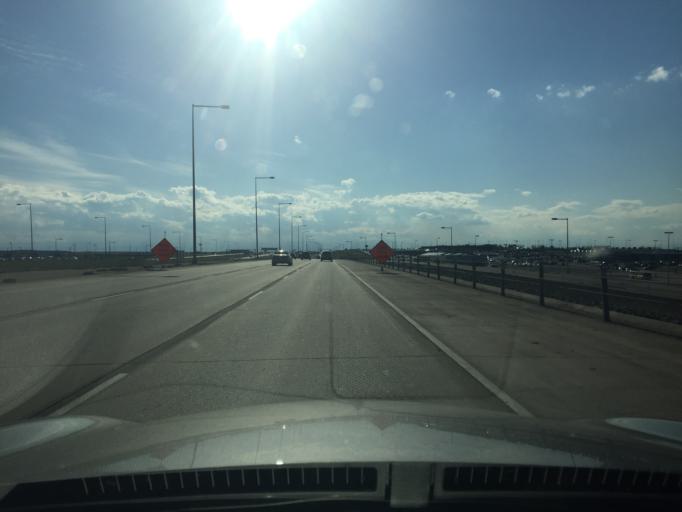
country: US
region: Colorado
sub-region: Adams County
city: Aurora
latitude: 39.8343
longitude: -104.6945
